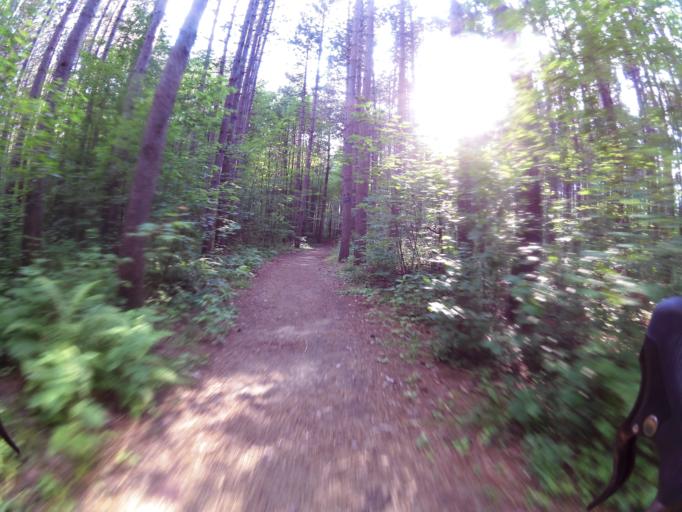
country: CA
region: Ontario
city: Ottawa
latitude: 45.3236
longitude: -75.7304
